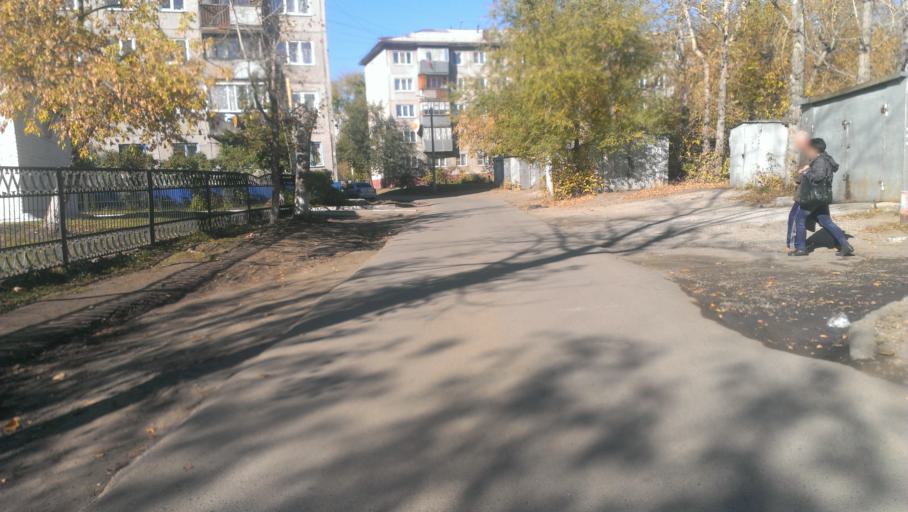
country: RU
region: Altai Krai
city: Novosilikatnyy
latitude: 53.3645
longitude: 83.6791
